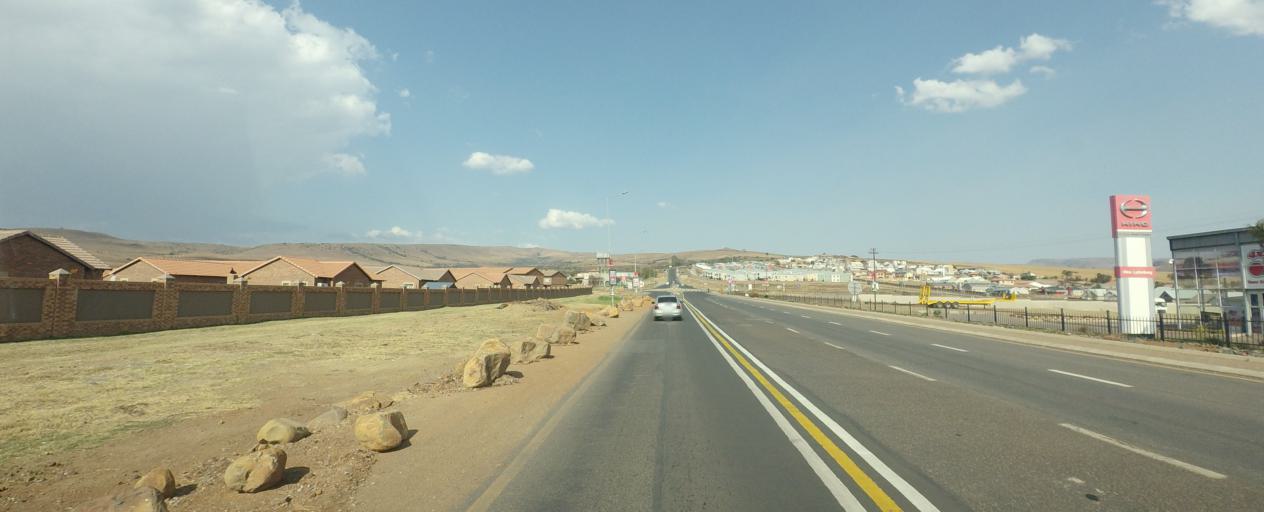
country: ZA
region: Mpumalanga
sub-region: Ehlanzeni District
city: Lydenburg
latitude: -25.1036
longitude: 30.4798
